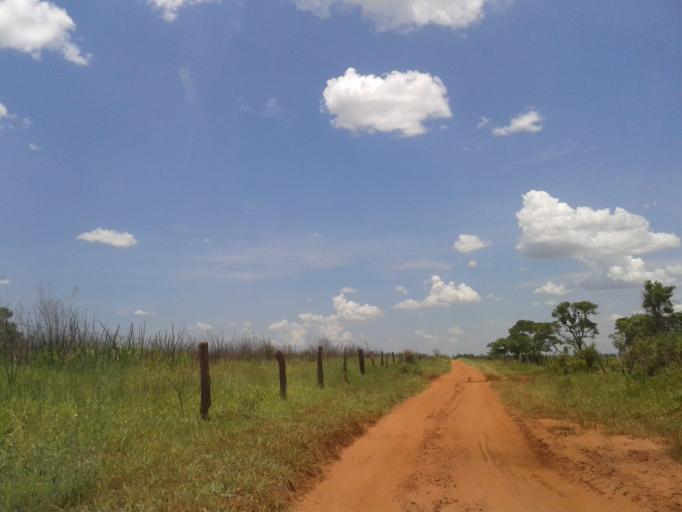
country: BR
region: Minas Gerais
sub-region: Santa Vitoria
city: Santa Vitoria
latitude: -19.2255
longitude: -50.4488
